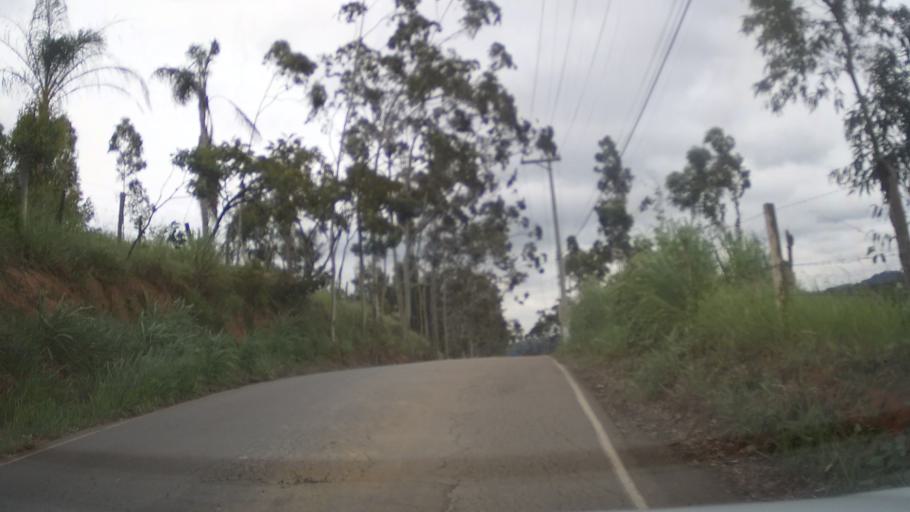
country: BR
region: Sao Paulo
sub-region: Vinhedo
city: Vinhedo
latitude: -23.0724
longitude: -47.0304
